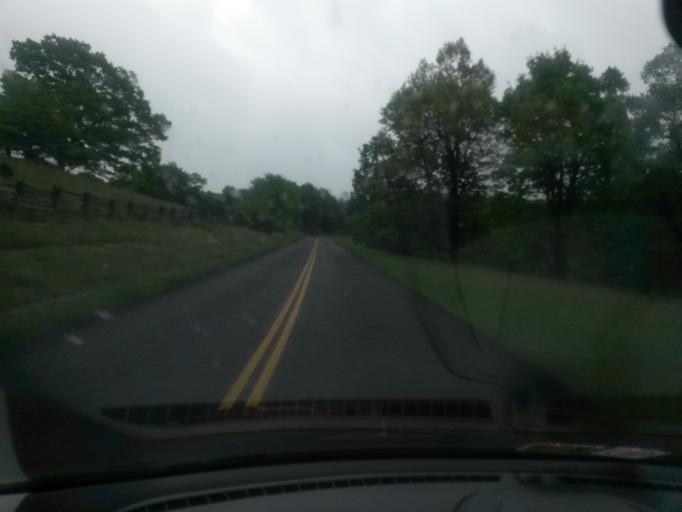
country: US
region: Virginia
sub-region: Floyd County
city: Floyd
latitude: 36.8294
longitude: -80.3462
